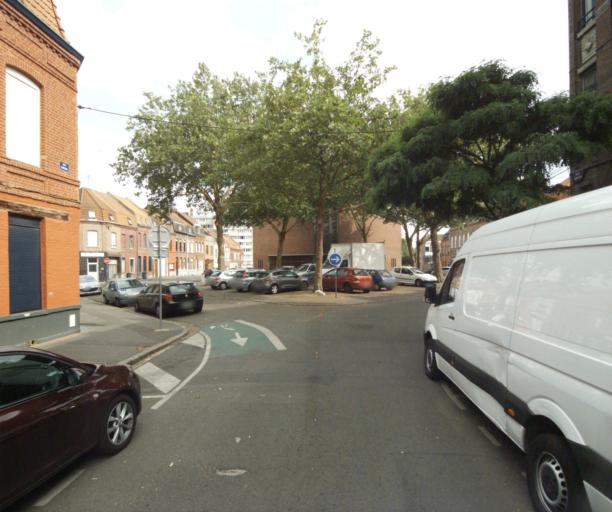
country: FR
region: Nord-Pas-de-Calais
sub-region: Departement du Nord
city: Croix
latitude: 50.6882
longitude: 3.1603
